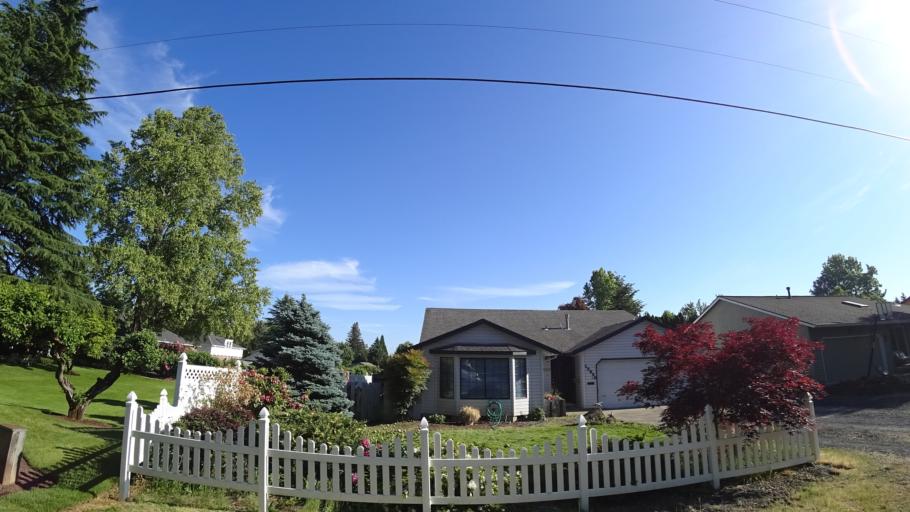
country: US
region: Oregon
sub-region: Washington County
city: Beaverton
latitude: 45.4602
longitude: -122.8090
